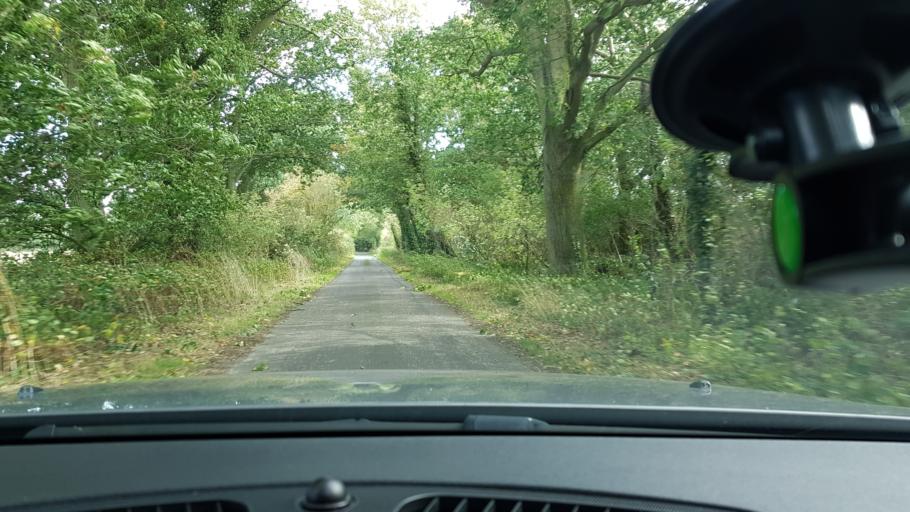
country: GB
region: England
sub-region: West Berkshire
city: Hungerford
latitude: 51.4252
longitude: -1.4958
